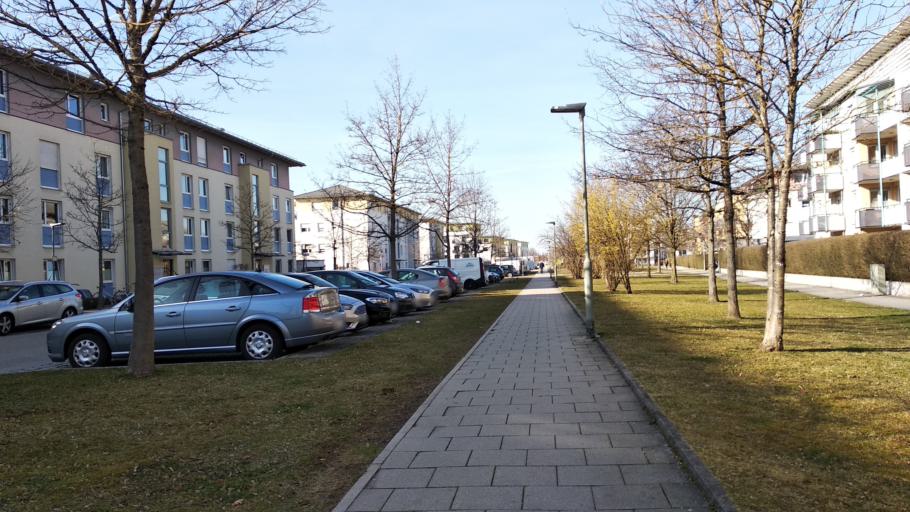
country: DE
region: Bavaria
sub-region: Upper Bavaria
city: Unterhaching
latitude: 48.0683
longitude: 11.6146
